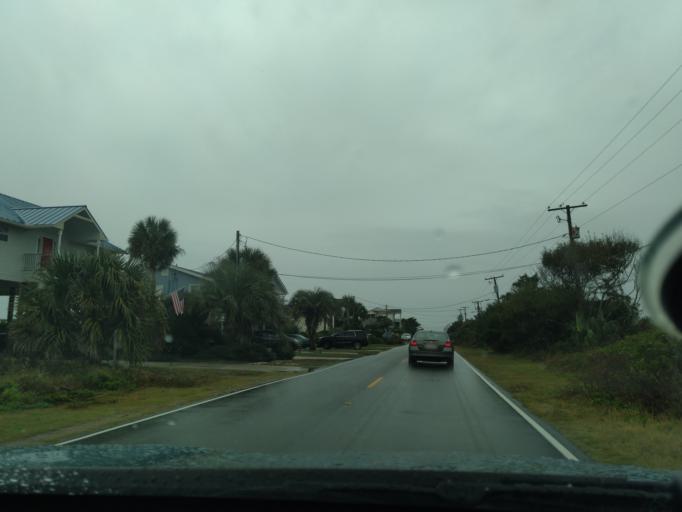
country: US
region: South Carolina
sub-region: Charleston County
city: Folly Beach
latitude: 32.6736
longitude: -79.9024
